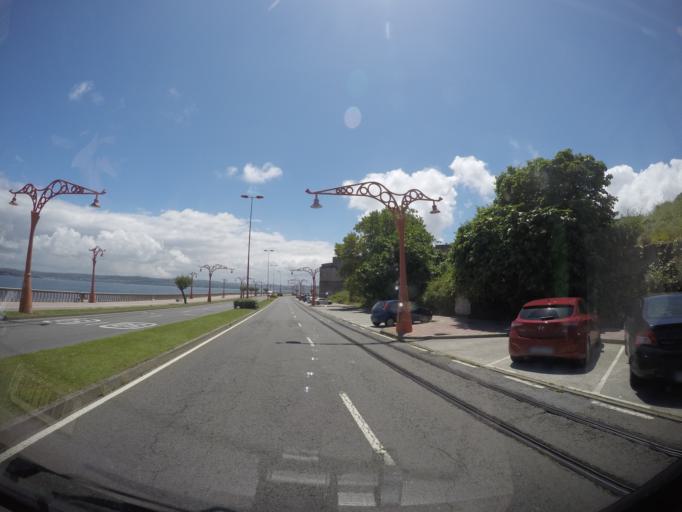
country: ES
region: Galicia
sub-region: Provincia da Coruna
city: A Coruna
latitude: 43.3782
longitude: -8.3944
